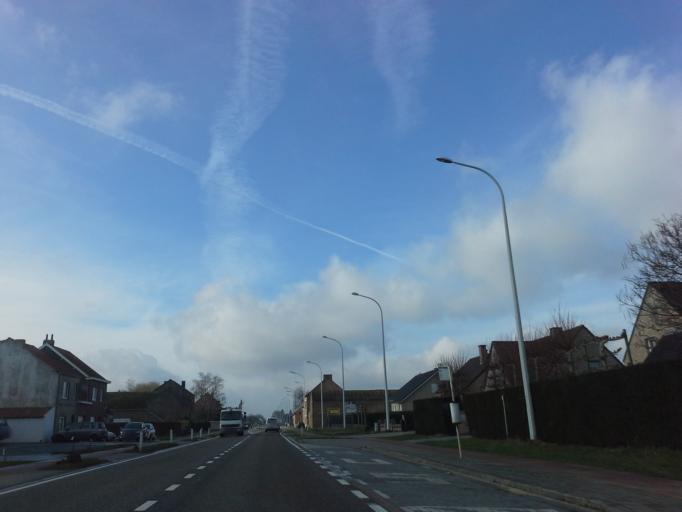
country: BE
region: Flanders
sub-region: Provincie Vlaams-Brabant
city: Landen
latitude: 50.8015
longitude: 5.0446
